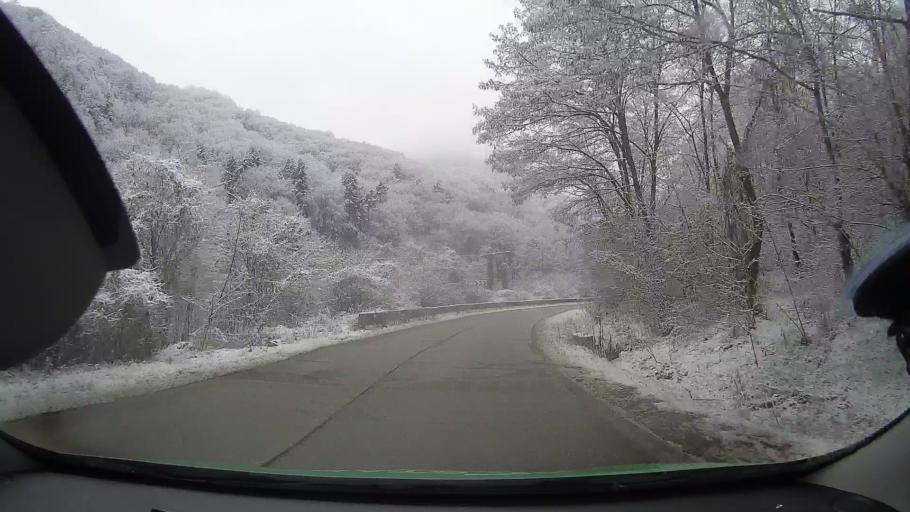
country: RO
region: Cluj
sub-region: Comuna Moldovenesti
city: Moldovenesti
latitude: 46.5040
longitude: 23.6364
